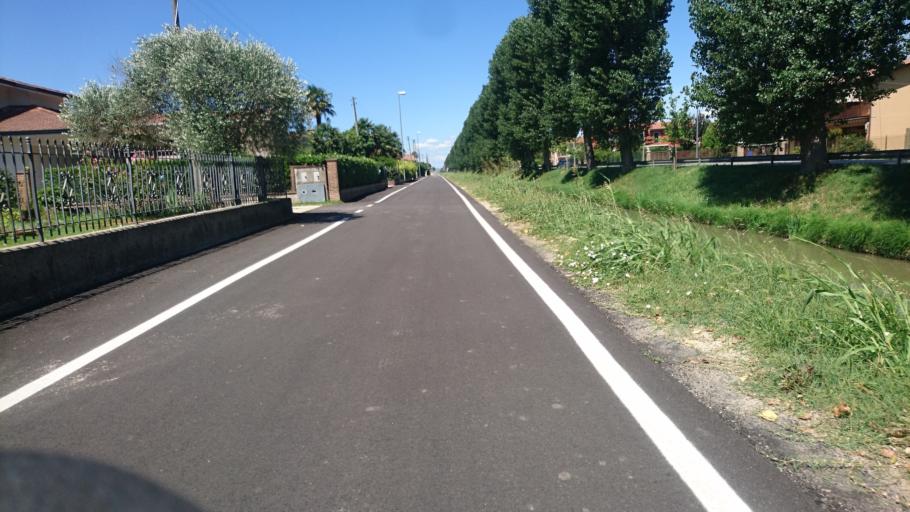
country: IT
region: Veneto
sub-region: Provincia di Padova
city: Sant'Angelo di Piove di Sacco
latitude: 45.3029
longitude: 12.0126
